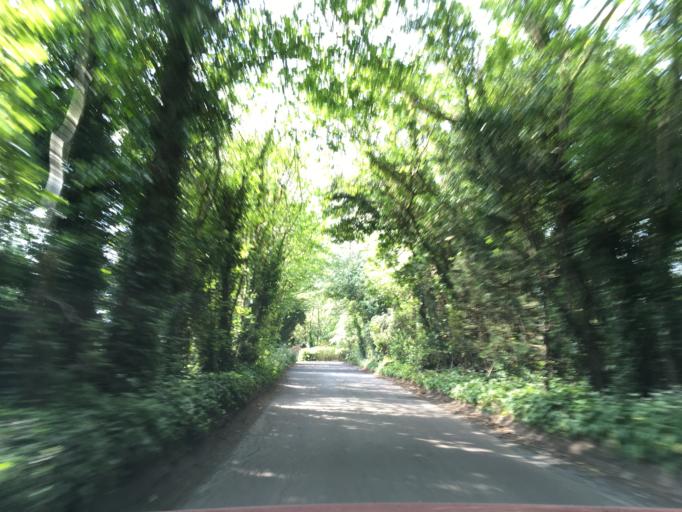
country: GB
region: England
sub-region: North Somerset
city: Butcombe
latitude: 51.3962
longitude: -2.7144
